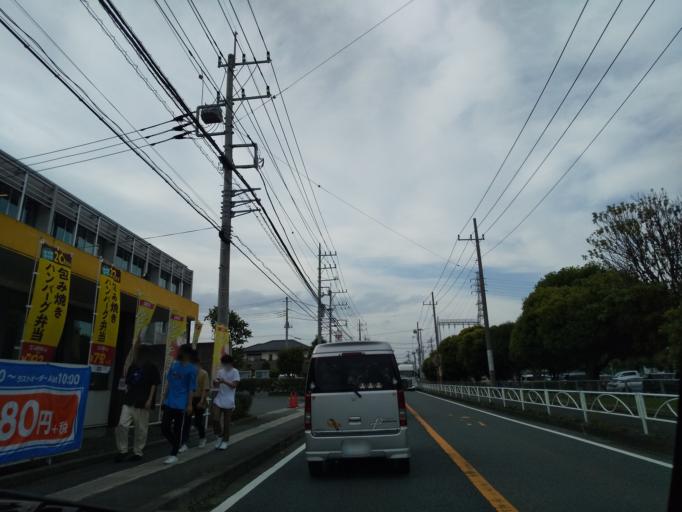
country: JP
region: Kanagawa
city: Zama
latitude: 35.4896
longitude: 139.3401
